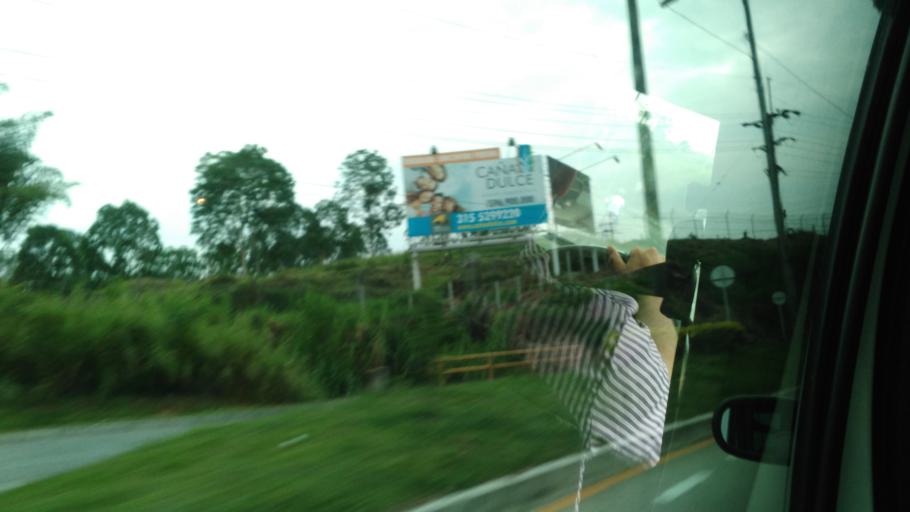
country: CO
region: Risaralda
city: Pereira
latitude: 4.8094
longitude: -75.7334
